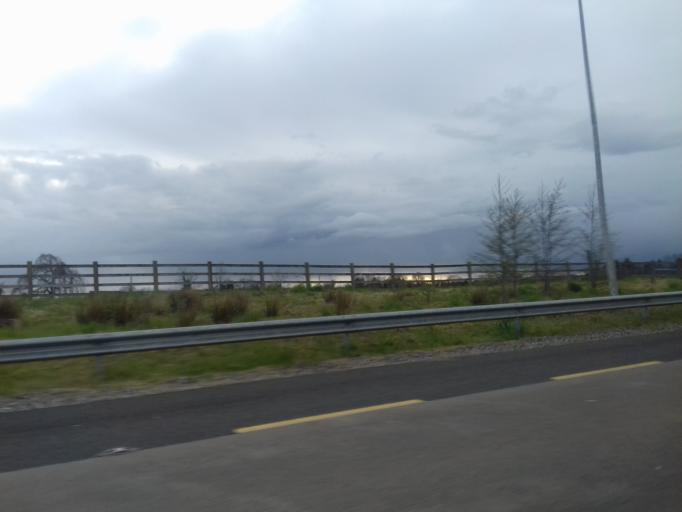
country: IE
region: Ulster
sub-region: An Cabhan
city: Belturbet
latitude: 54.0974
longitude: -7.4601
